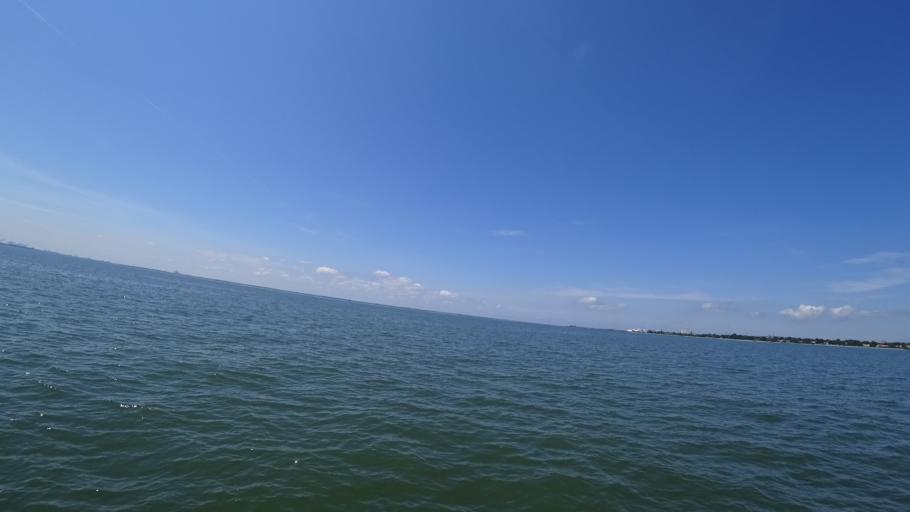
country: US
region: Virginia
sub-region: City of Newport News
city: Newport News
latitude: 36.9815
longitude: -76.3831
